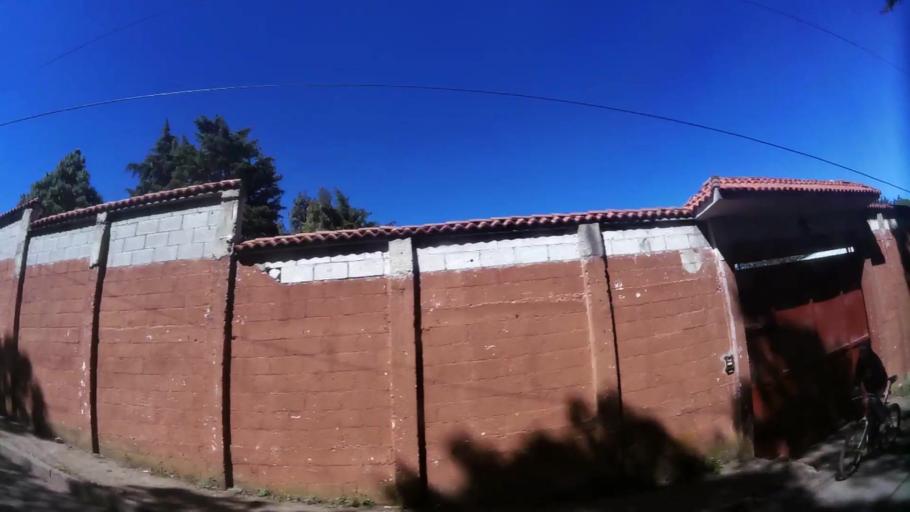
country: GT
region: Guatemala
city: San Jose Pinula
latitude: 14.5288
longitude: -90.4172
